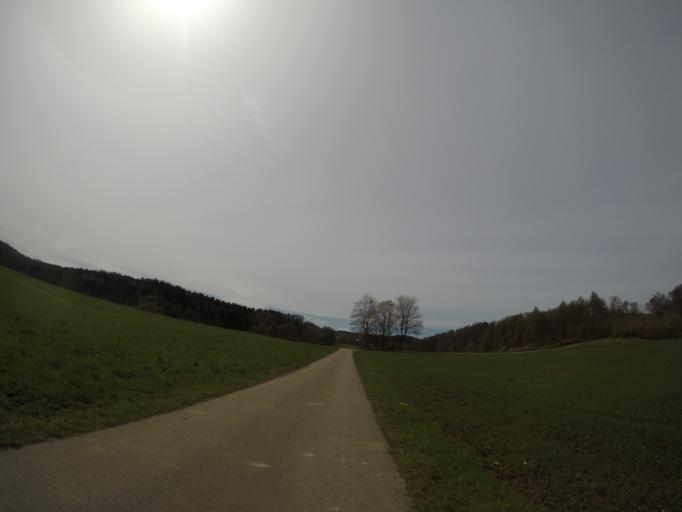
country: DE
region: Baden-Wuerttemberg
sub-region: Regierungsbezirk Stuttgart
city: Neidlingen
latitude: 48.5380
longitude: 9.5550
